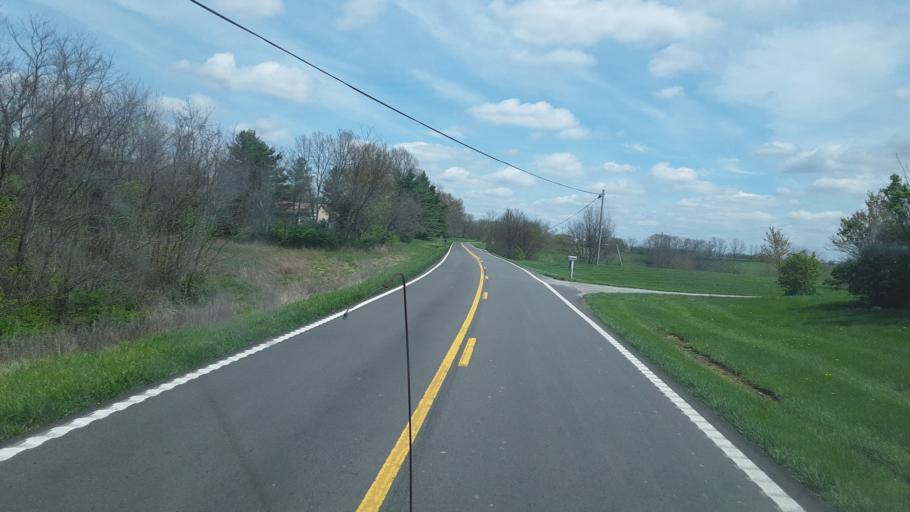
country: US
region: Kentucky
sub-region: Grant County
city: Dry Ridge
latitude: 38.6627
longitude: -84.6523
